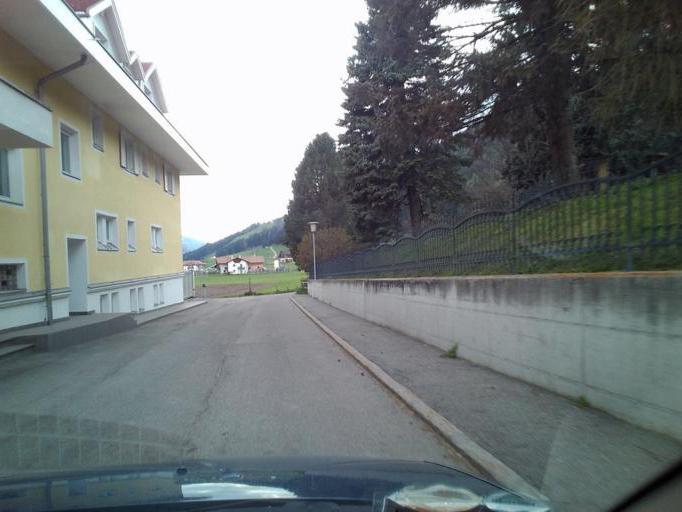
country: IT
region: Trentino-Alto Adige
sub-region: Bolzano
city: Villabassa
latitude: 46.7402
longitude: 12.1671
